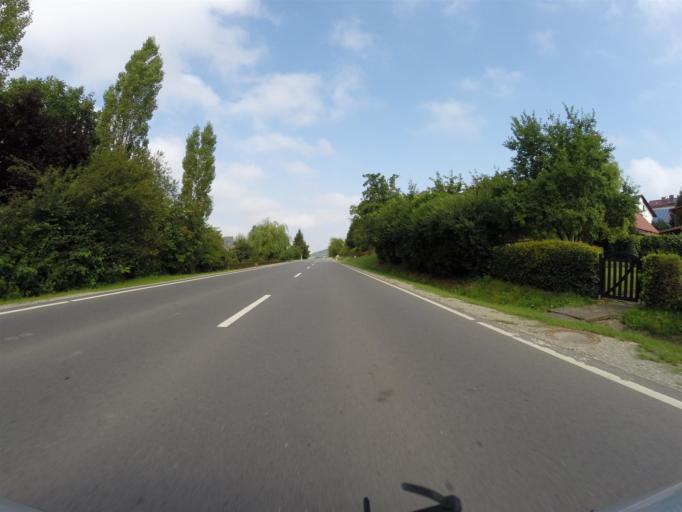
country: DE
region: Hesse
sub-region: Regierungsbezirk Kassel
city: Weissenborn
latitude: 51.0960
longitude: 10.0901
